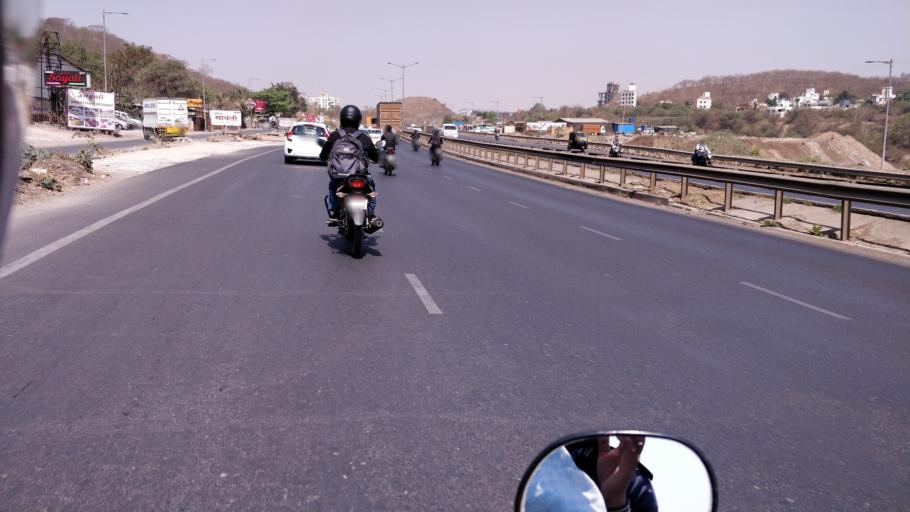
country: IN
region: Maharashtra
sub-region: Pune Division
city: Shivaji Nagar
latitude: 18.5419
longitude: 73.7776
